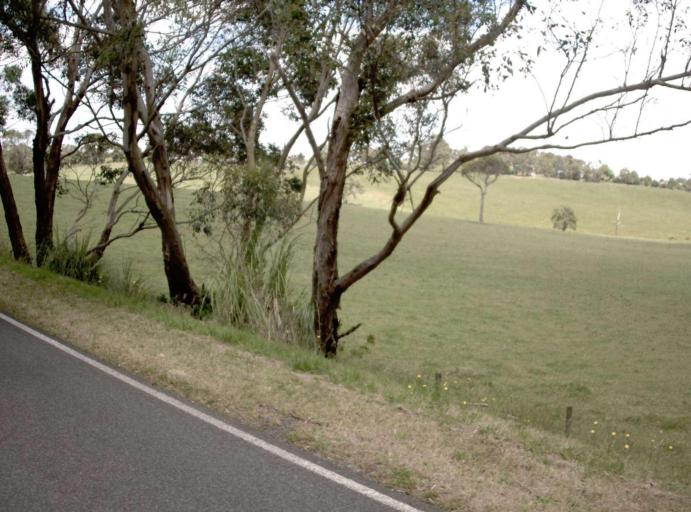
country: AU
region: Victoria
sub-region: Bass Coast
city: North Wonthaggi
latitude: -38.5789
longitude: 146.0235
